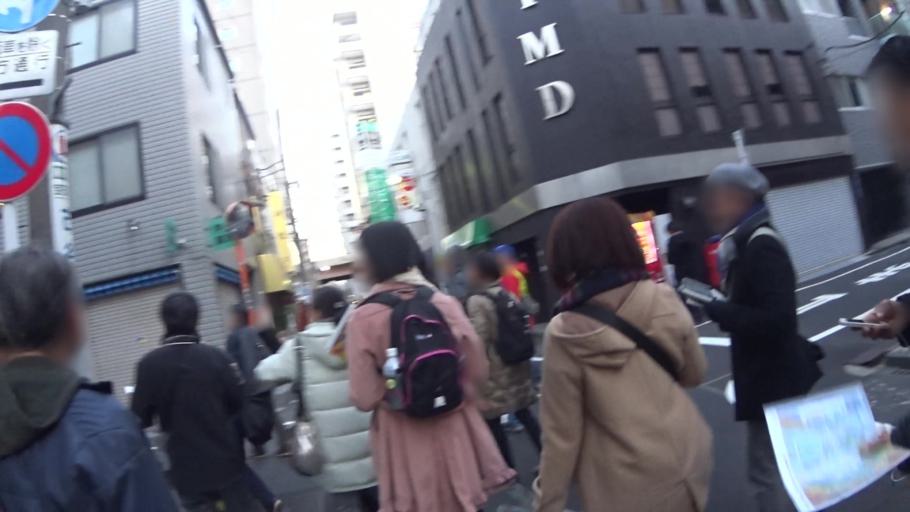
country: JP
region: Tokyo
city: Tokyo
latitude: 35.7051
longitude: 139.7760
